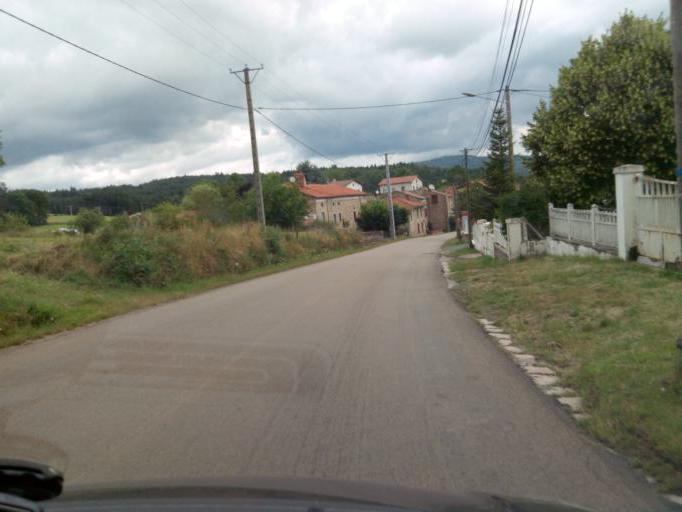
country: FR
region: Rhone-Alpes
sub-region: Departement de la Loire
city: Usson-en-Forez
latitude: 45.3944
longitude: 3.9443
